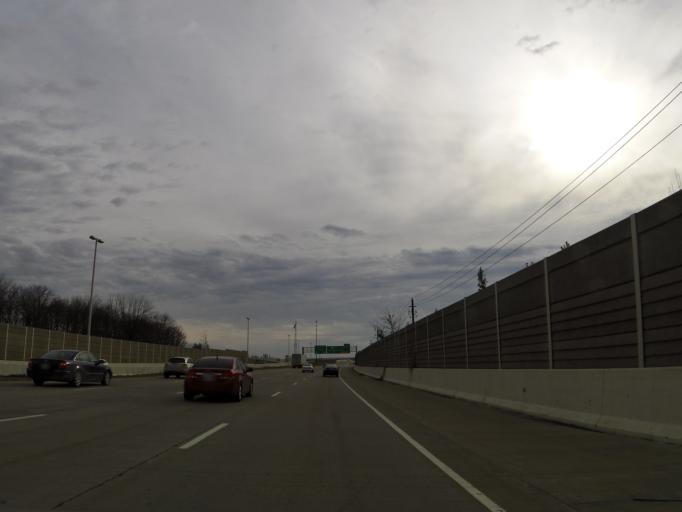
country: US
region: Indiana
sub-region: Marion County
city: Speedway
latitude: 39.8095
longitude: -86.2823
